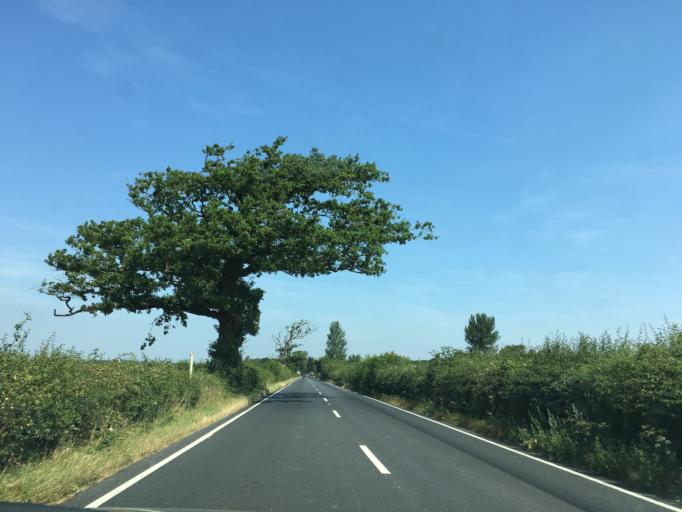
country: GB
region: England
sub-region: Isle of Wight
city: Newport
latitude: 50.7114
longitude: -1.2457
